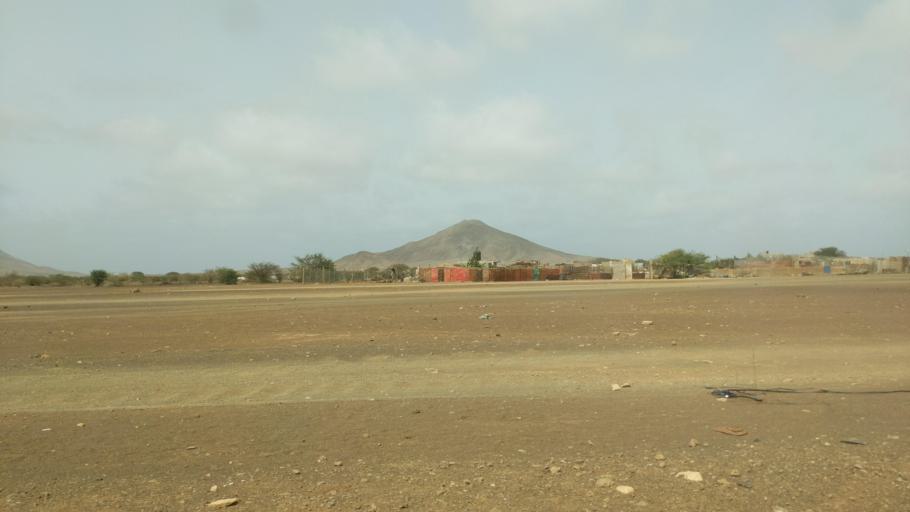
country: CV
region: Sal
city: Espargos
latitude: 16.7746
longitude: -22.9480
